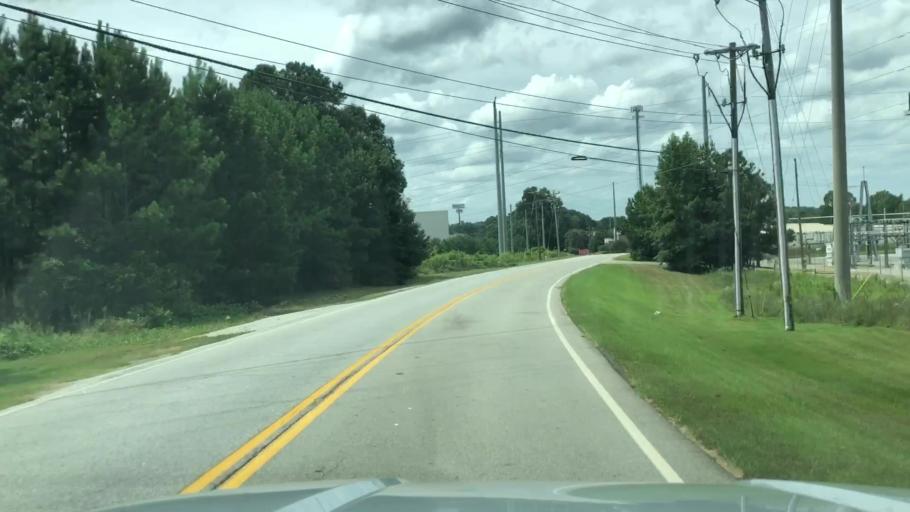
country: US
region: Georgia
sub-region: Gwinnett County
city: Suwanee
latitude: 34.0343
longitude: -84.0393
